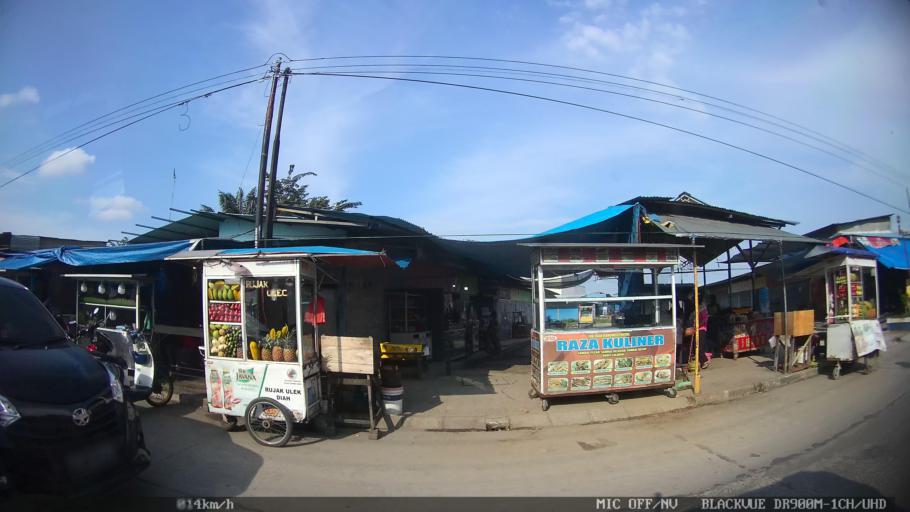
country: ID
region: North Sumatra
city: Medan
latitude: 3.5960
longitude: 98.7532
